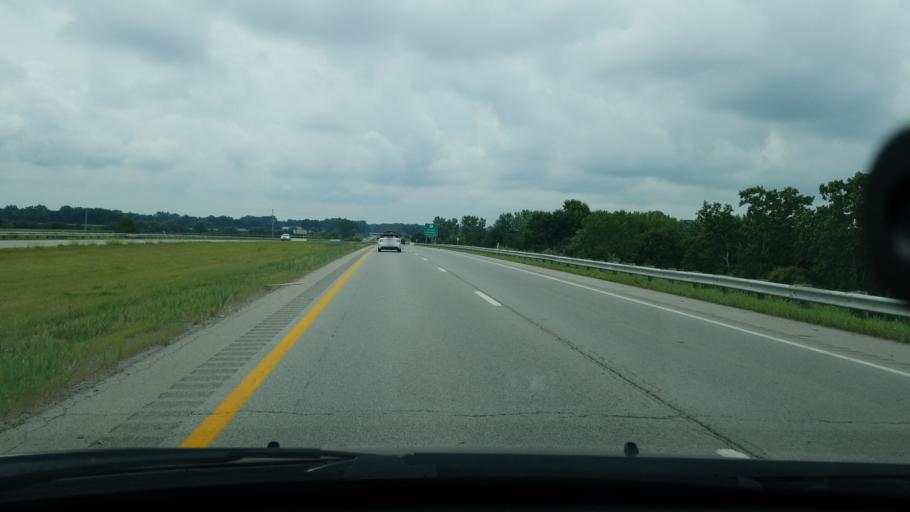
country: US
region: Ohio
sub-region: Erie County
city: Huron
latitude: 41.3912
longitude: -82.5742
